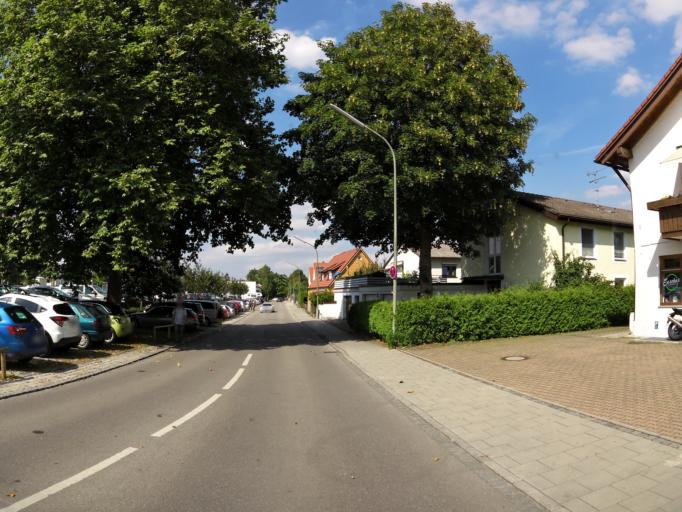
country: DE
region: Bavaria
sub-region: Upper Bavaria
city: Herrsching am Ammersee
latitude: 47.9991
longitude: 11.1712
